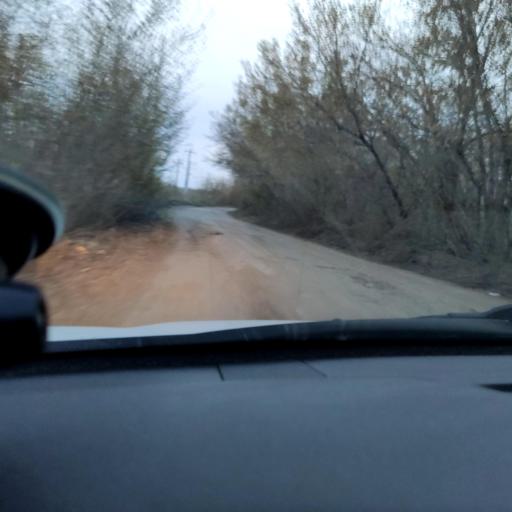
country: RU
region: Samara
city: Smyshlyayevka
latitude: 53.1522
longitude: 50.3902
